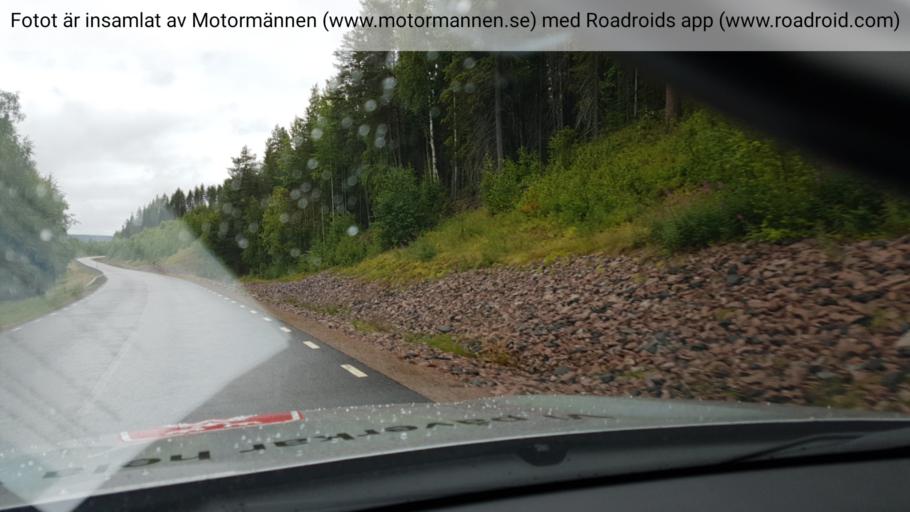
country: SE
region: Norrbotten
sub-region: Gallivare Kommun
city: Gaellivare
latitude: 66.6250
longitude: 20.4205
